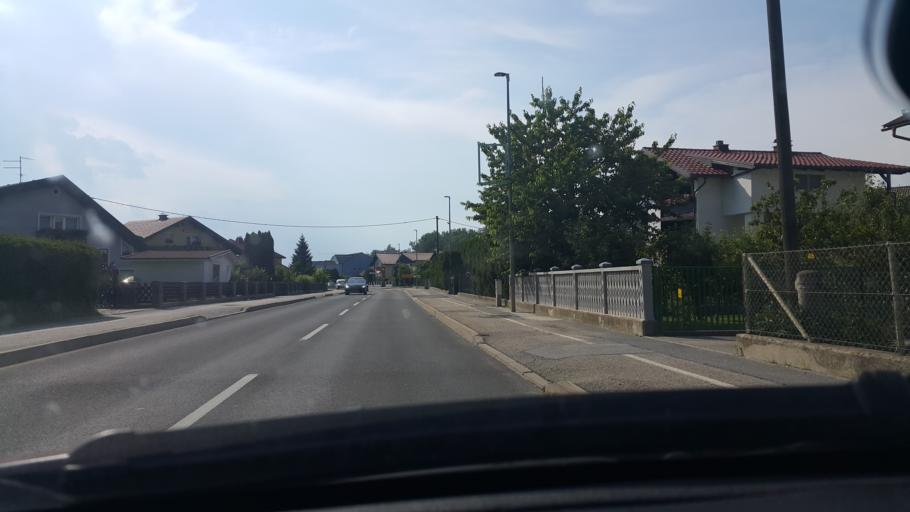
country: SI
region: Duplek
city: Spodnji Duplek
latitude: 46.5058
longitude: 15.7403
